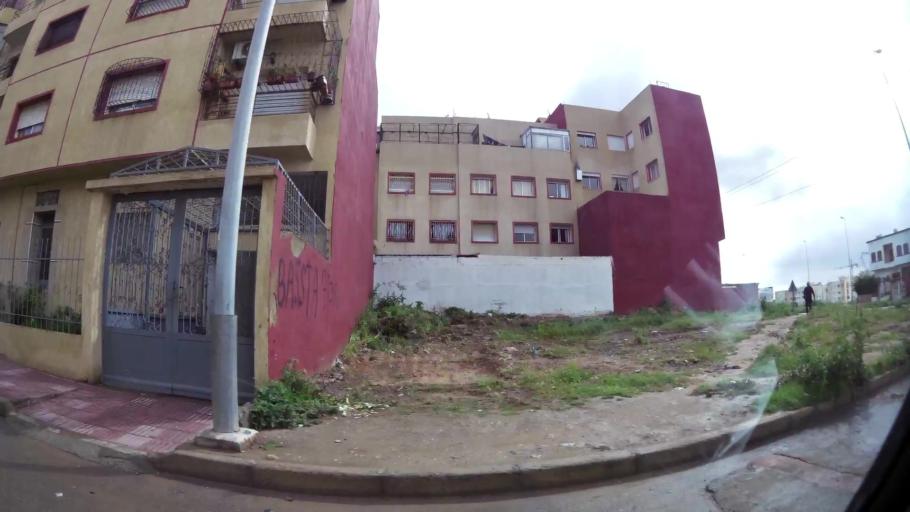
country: MA
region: Grand Casablanca
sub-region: Mediouna
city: Tit Mellil
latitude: 33.5437
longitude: -7.4817
